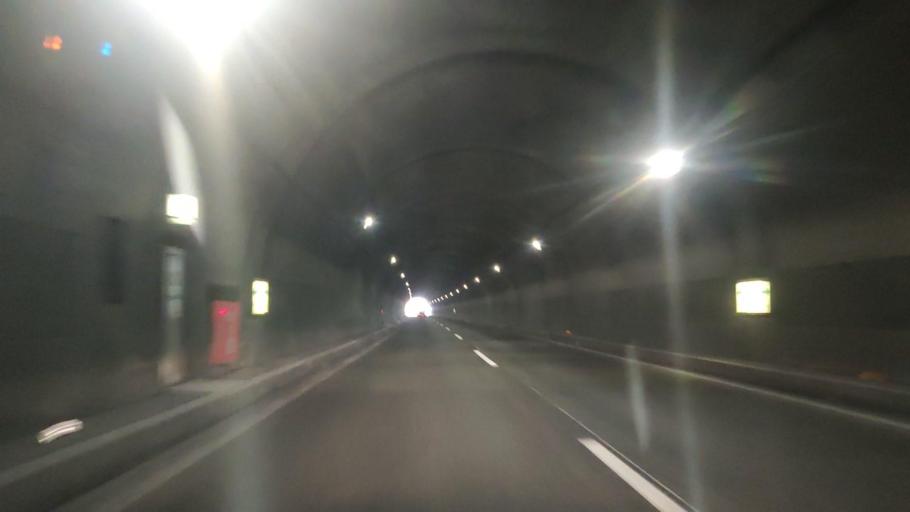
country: JP
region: Oita
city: Beppu
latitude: 33.2764
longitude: 131.3436
